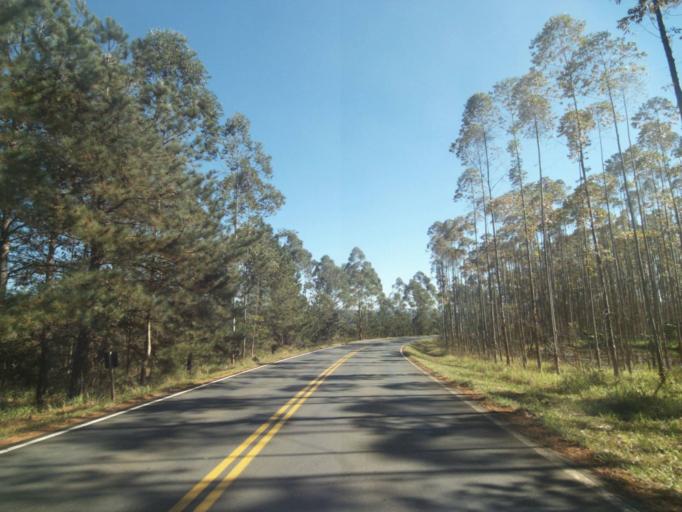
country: BR
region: Parana
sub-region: Tibagi
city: Tibagi
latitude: -24.4574
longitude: -50.5432
